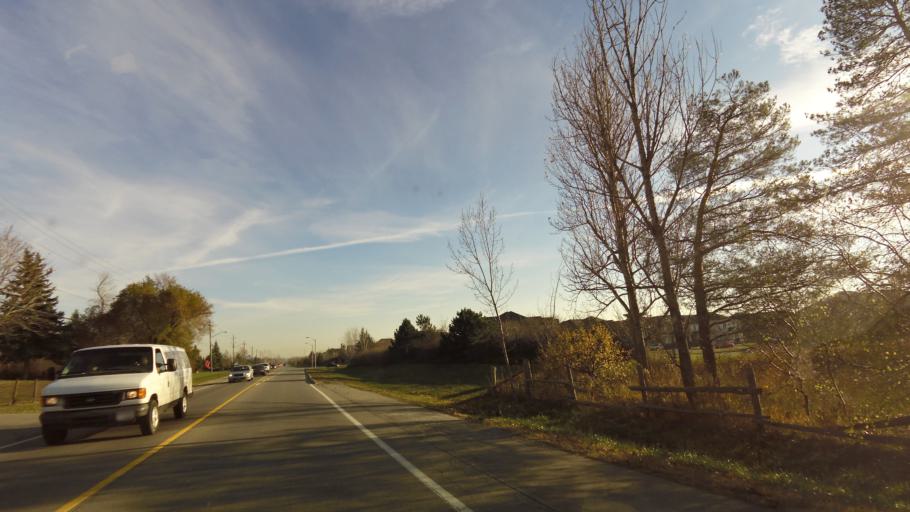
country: CA
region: Ontario
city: Brampton
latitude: 43.7771
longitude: -79.7168
